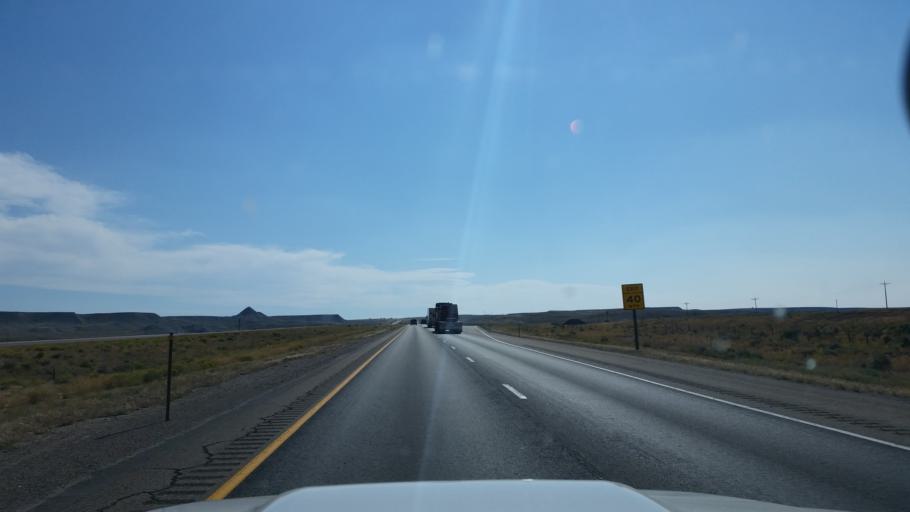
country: US
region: Wyoming
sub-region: Uinta County
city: Lyman
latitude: 41.5123
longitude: -109.9806
